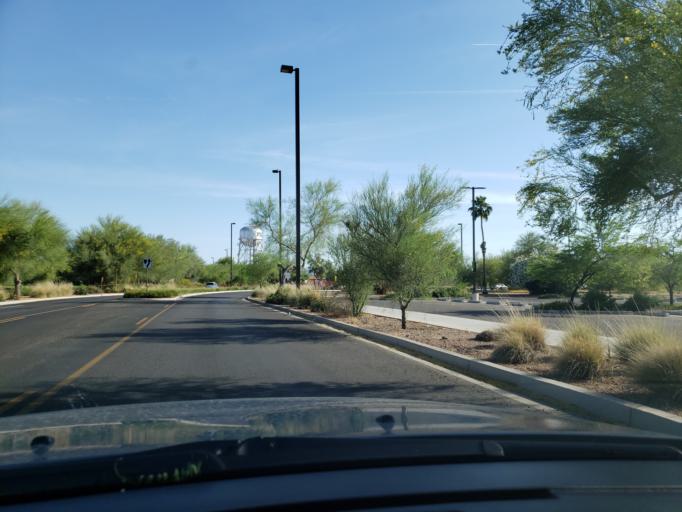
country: US
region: Arizona
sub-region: Maricopa County
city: Queen Creek
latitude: 33.3083
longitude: -111.6808
